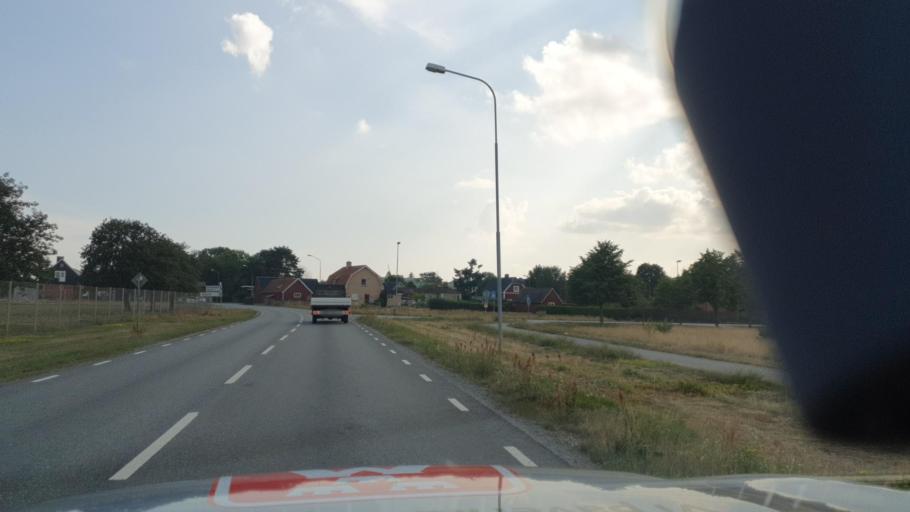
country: SE
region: Blekinge
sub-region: Solvesborgs Kommun
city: Soelvesborg
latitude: 56.0502
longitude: 14.6832
